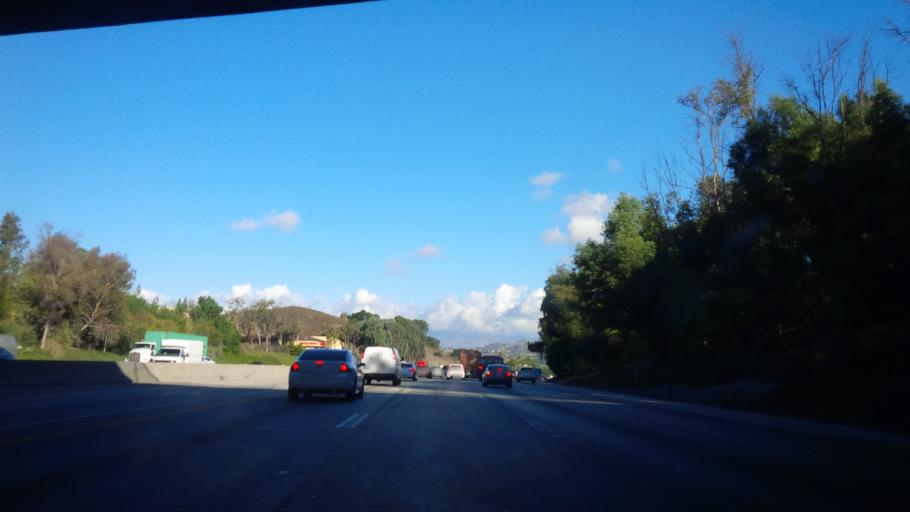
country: US
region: California
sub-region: Los Angeles County
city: Walnut
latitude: 33.9845
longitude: -117.8427
